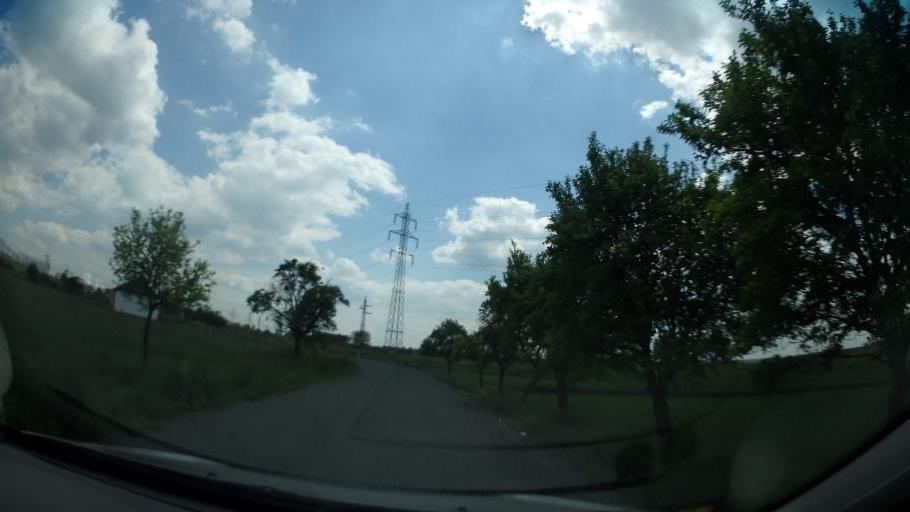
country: CZ
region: Vysocina
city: Rouchovany
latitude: 49.1070
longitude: 16.1092
